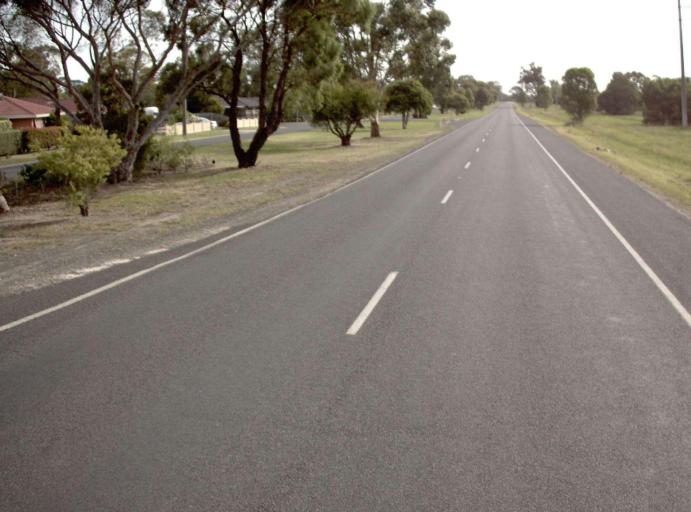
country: AU
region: Victoria
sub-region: Latrobe
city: Traralgon
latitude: -38.1223
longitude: 146.5719
